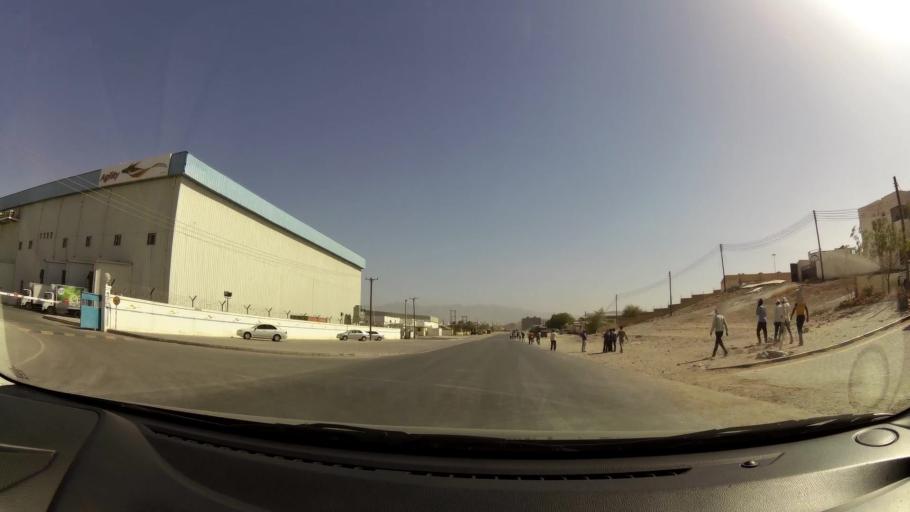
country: OM
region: Muhafazat Masqat
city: Bawshar
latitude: 23.5748
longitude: 58.3526
